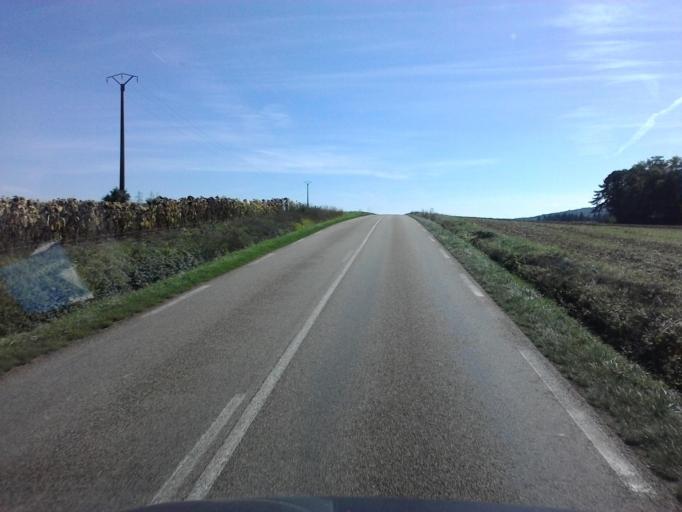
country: FR
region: Bourgogne
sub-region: Departement de l'Yonne
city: Joux-la-Ville
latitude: 47.5755
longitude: 3.8791
